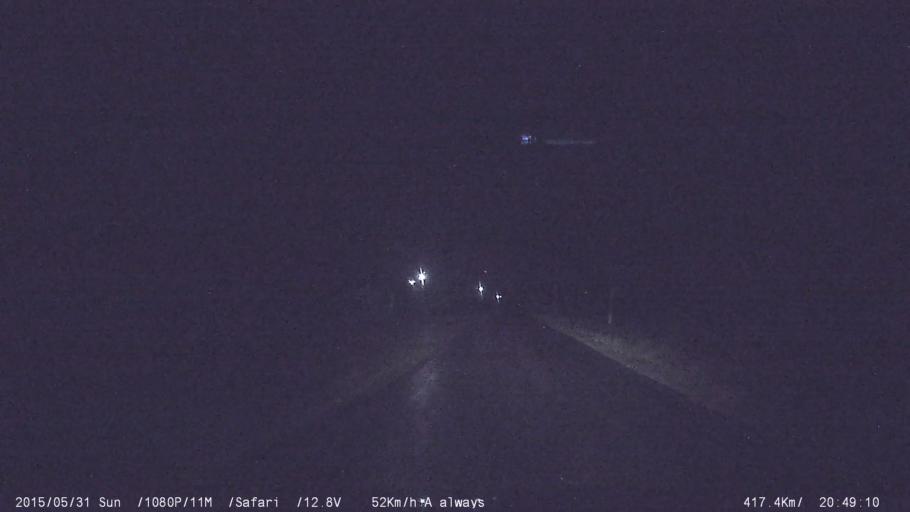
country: IN
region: Karnataka
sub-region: Ramanagara
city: Channapatna
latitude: 12.5759
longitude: 77.2185
